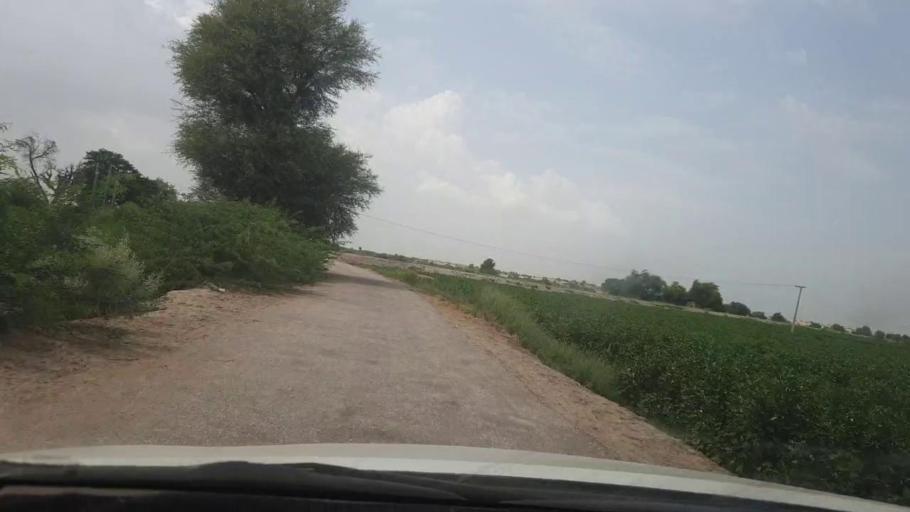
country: PK
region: Sindh
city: Kot Diji
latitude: 27.3105
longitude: 69.0119
